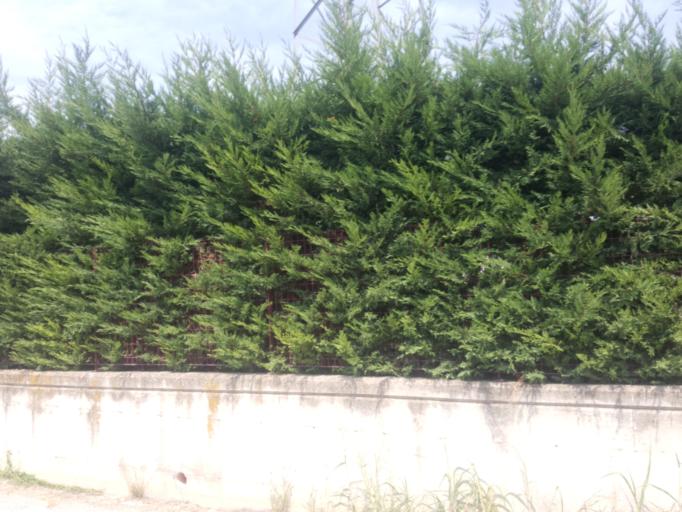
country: IT
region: Piedmont
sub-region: Provincia di Cuneo
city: Narzole
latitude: 44.5945
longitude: 7.8967
